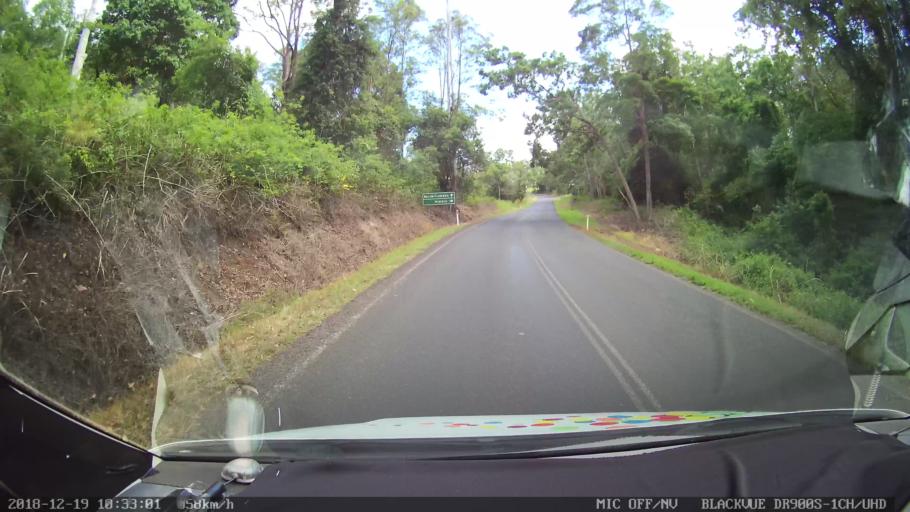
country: AU
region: New South Wales
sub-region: Lismore Municipality
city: Larnook
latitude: -28.5781
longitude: 153.1247
